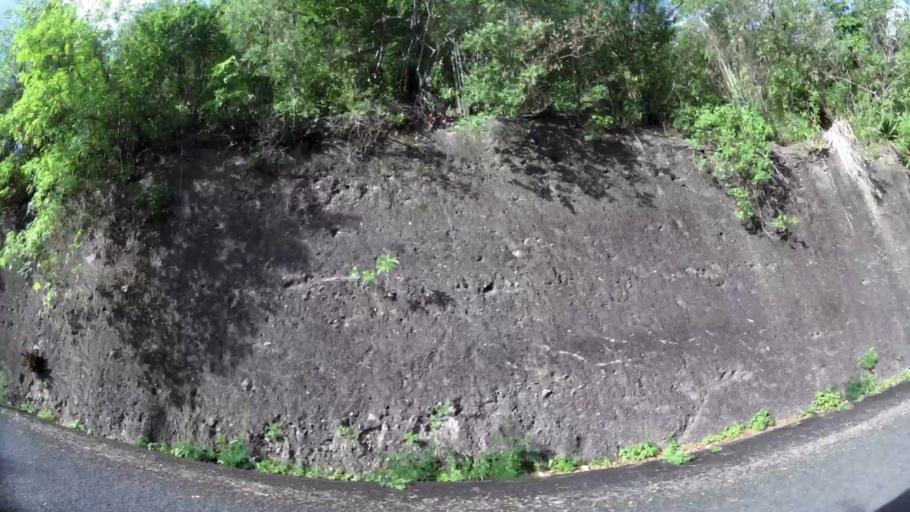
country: LC
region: Anse-la-Raye
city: Canaries
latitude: 13.9030
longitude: -61.0684
